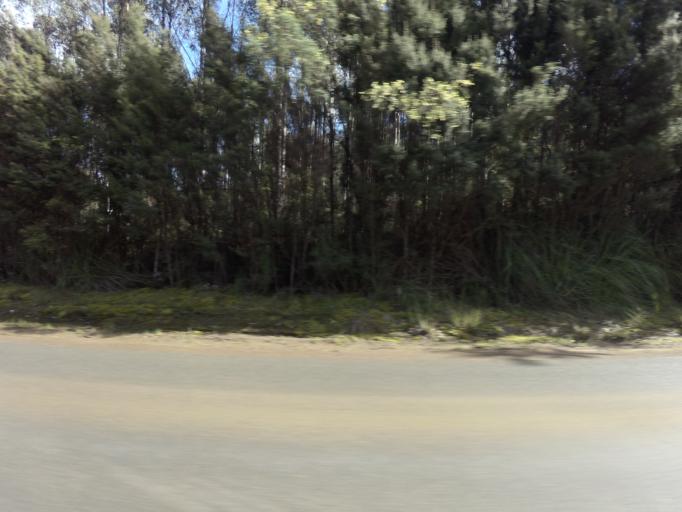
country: AU
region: Tasmania
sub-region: Huon Valley
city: Geeveston
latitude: -43.3491
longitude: 146.9601
